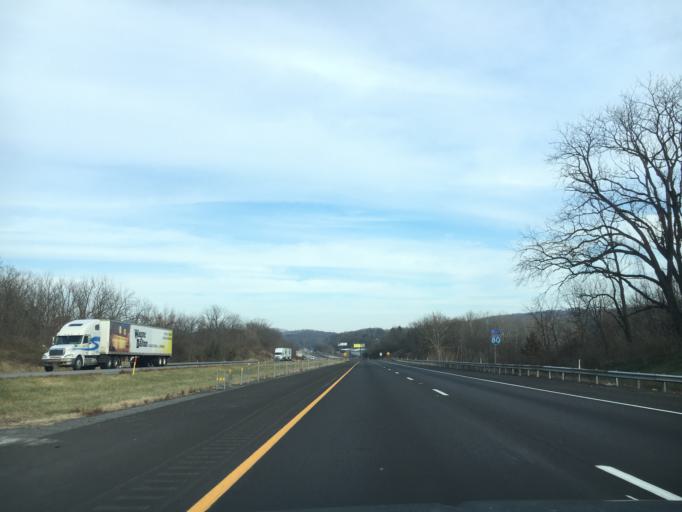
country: US
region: Pennsylvania
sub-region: Columbia County
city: Bloomsburg
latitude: 41.0156
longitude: -76.4821
